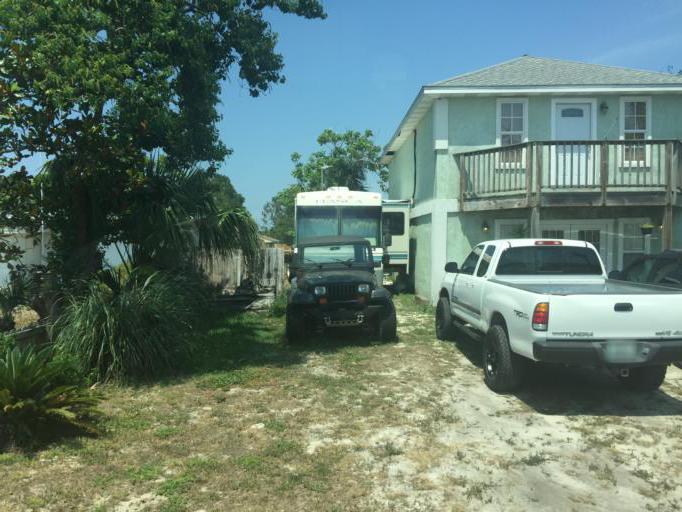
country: US
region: Florida
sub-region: Bay County
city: Lower Grand Lagoon
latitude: 30.1469
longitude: -85.7571
